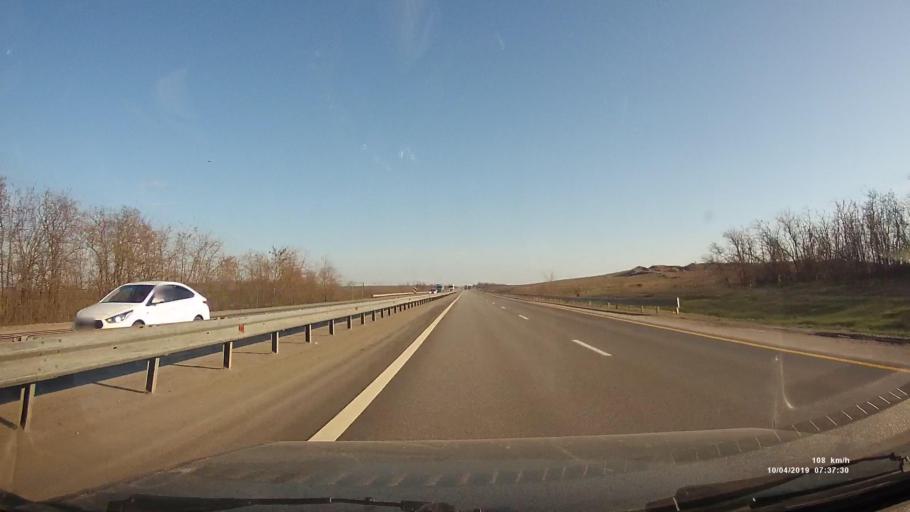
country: RU
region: Rostov
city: Likhoy
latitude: 48.0744
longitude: 40.2595
